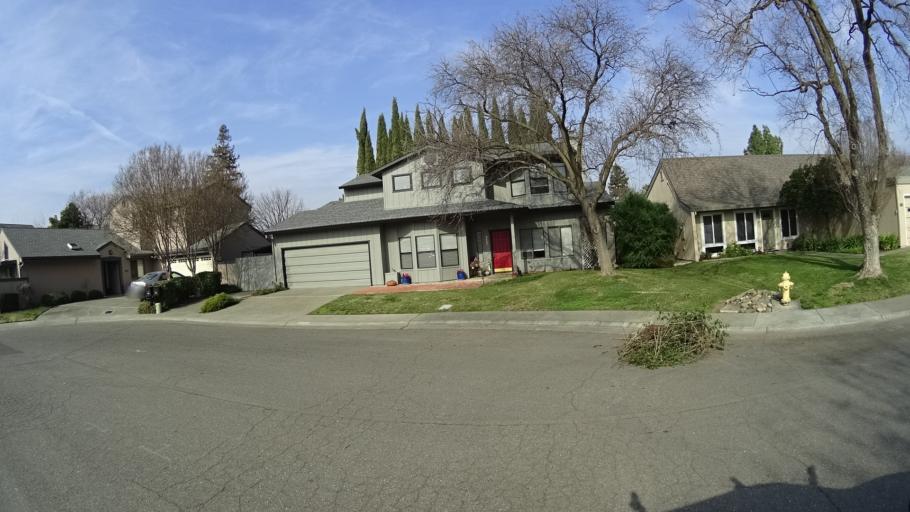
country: US
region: California
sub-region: Yolo County
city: Davis
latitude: 38.5683
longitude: -121.7488
